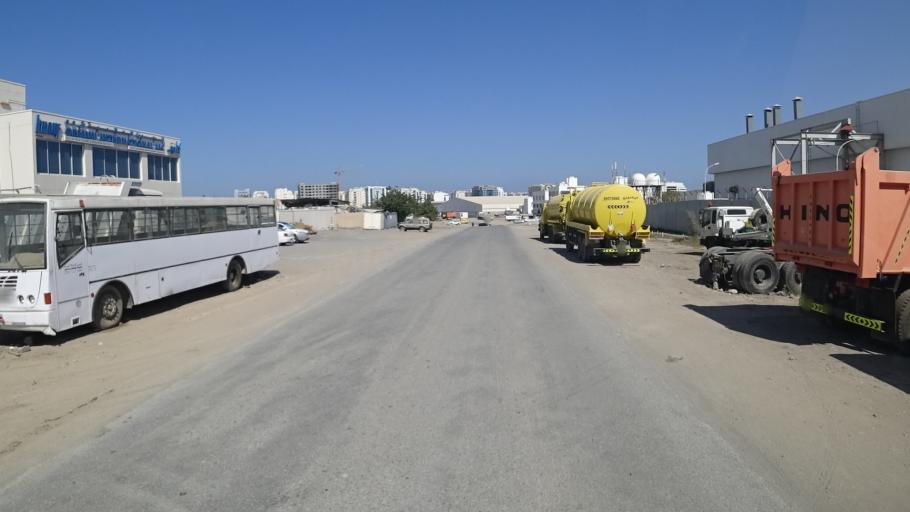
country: OM
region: Muhafazat Masqat
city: Bawshar
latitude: 23.5765
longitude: 58.3679
